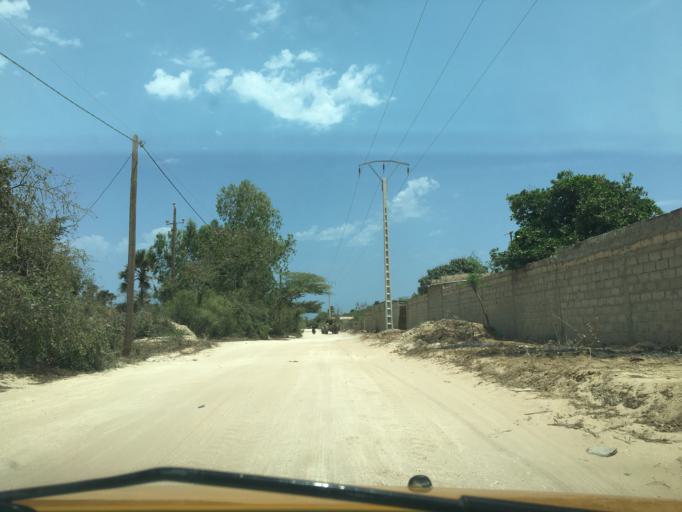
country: SN
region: Thies
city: Thies
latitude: 14.8237
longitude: -17.2044
